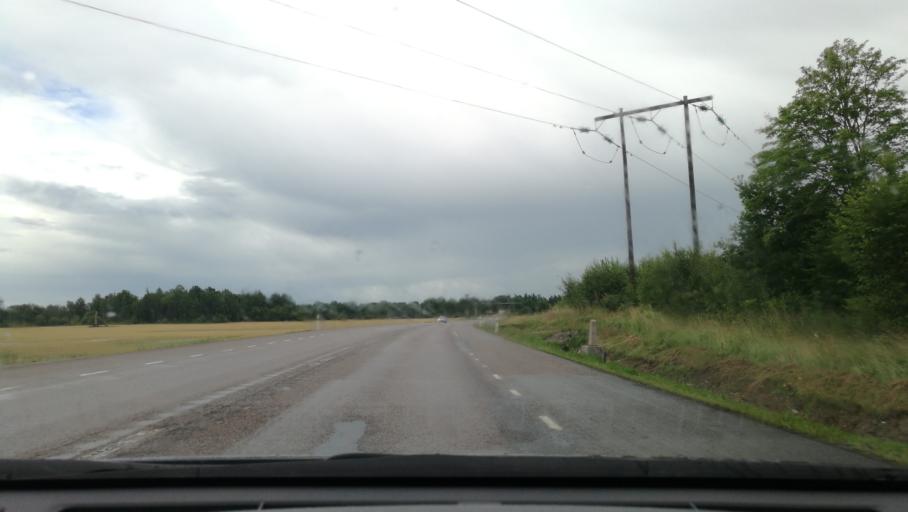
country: SE
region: Vaestmanland
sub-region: Kopings Kommun
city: Koping
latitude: 59.4561
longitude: 16.0211
